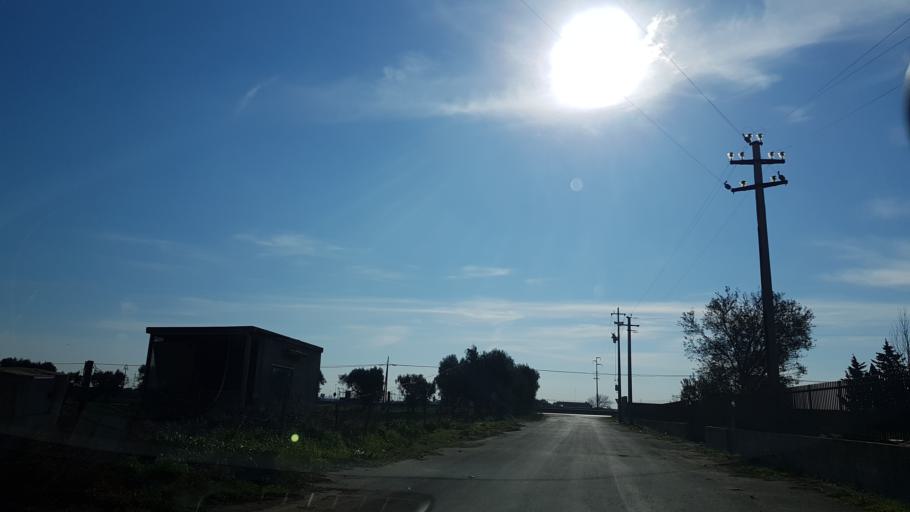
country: IT
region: Apulia
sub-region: Provincia di Brindisi
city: Brindisi
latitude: 40.6088
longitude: 17.8876
